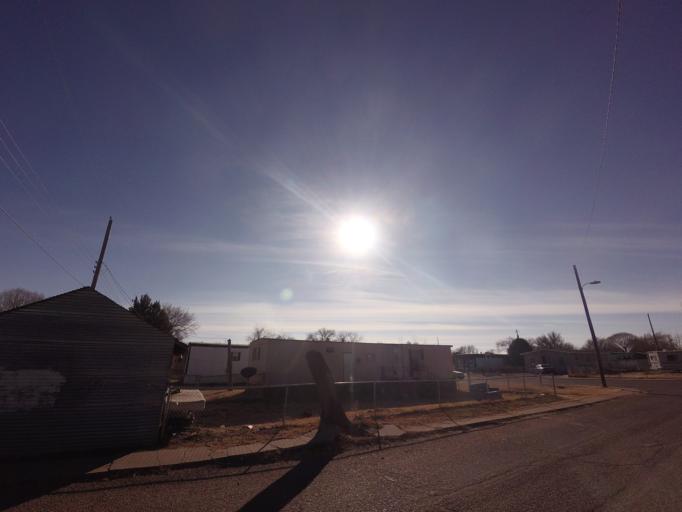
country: US
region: New Mexico
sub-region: Curry County
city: Clovis
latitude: 34.3878
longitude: -103.2005
